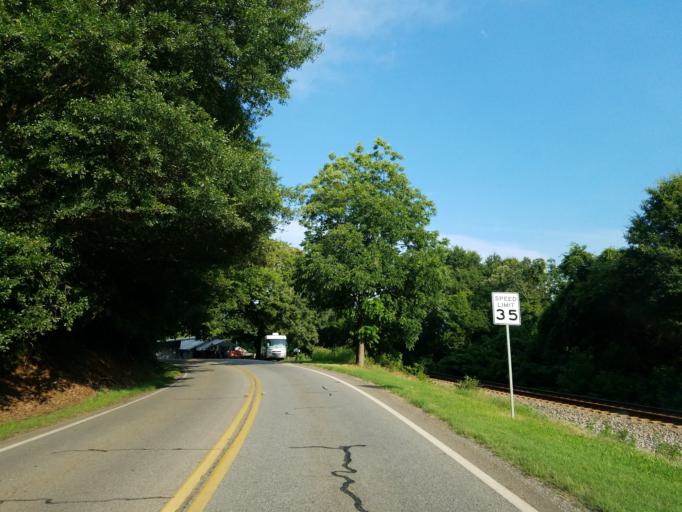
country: US
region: Georgia
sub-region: Bartow County
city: Cartersville
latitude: 34.1541
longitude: -84.7876
